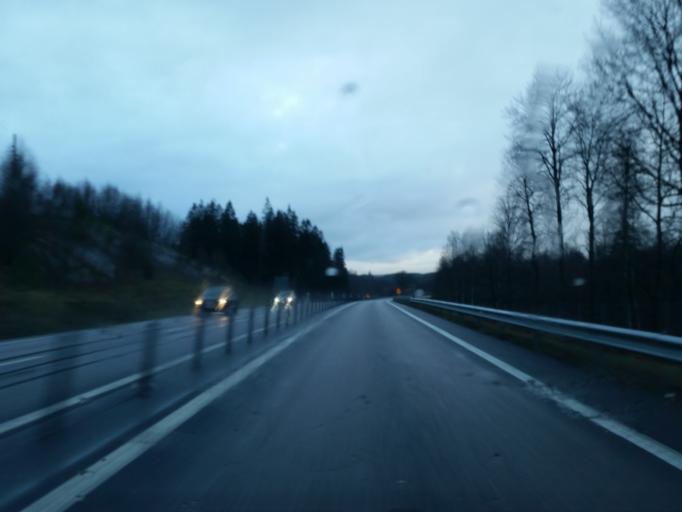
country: SE
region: Vaestra Goetaland
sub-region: Boras Kommun
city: Ganghester
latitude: 57.6762
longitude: 12.9812
